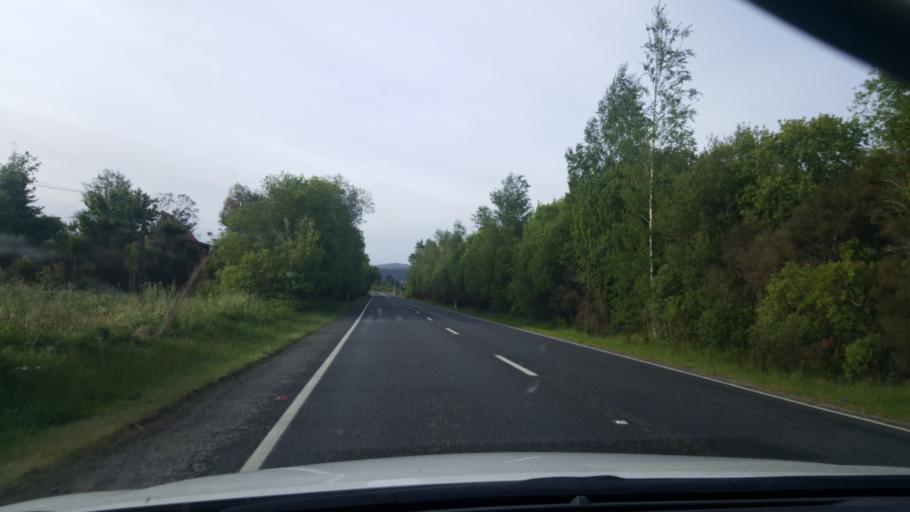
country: NZ
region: Waikato
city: Turangi
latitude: -38.9676
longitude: 175.7680
